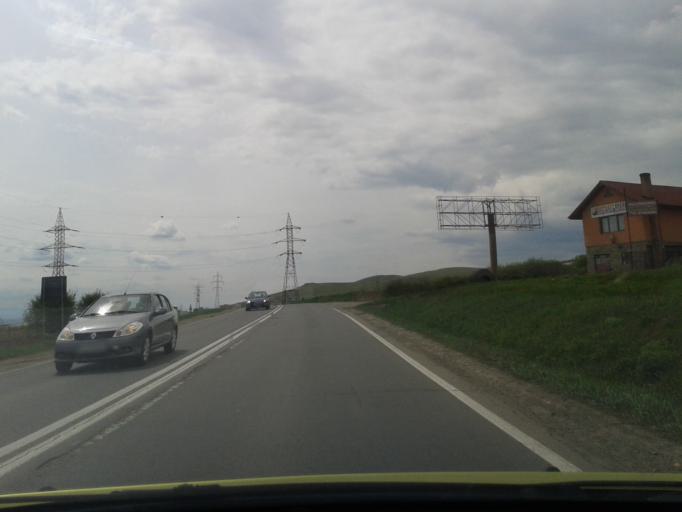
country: RO
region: Alba
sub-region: Comuna Santimbru
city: Santimbru
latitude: 46.1357
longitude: 23.6329
